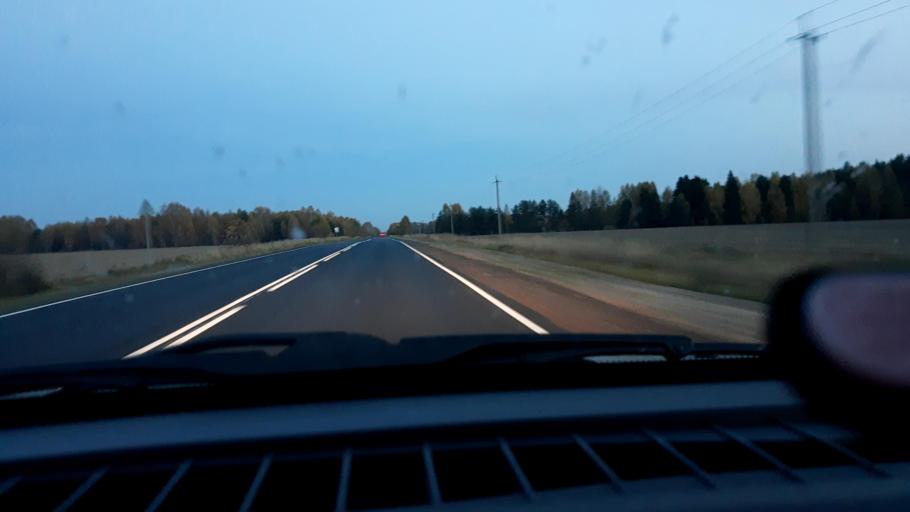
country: RU
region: Nizjnij Novgorod
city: Novaya Balakhna
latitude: 56.5962
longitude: 43.6458
